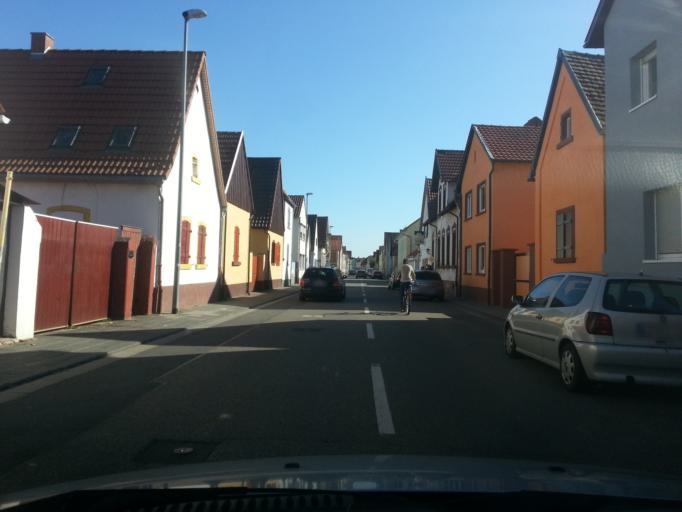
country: DE
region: Rheinland-Pfalz
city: Schifferstadt
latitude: 49.3883
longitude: 8.3780
